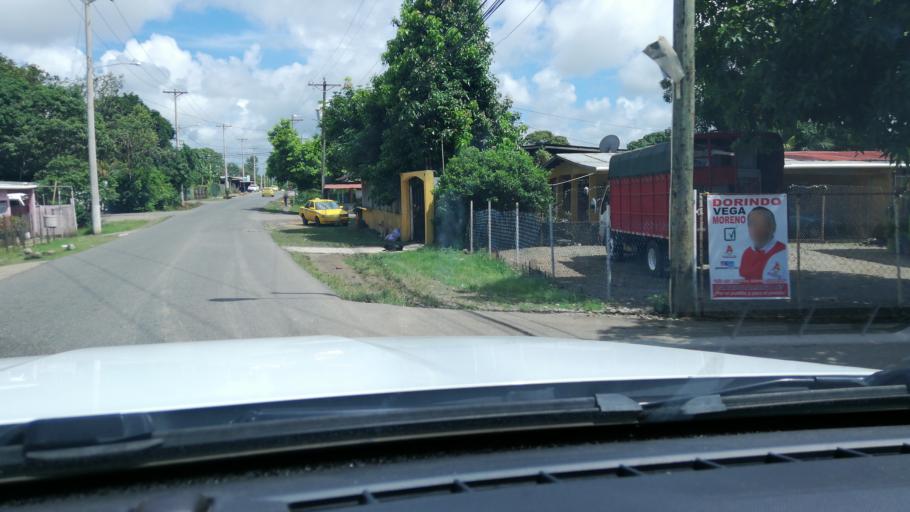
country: PA
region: Panama
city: Cabra Numero Uno
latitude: 9.1090
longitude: -79.3416
